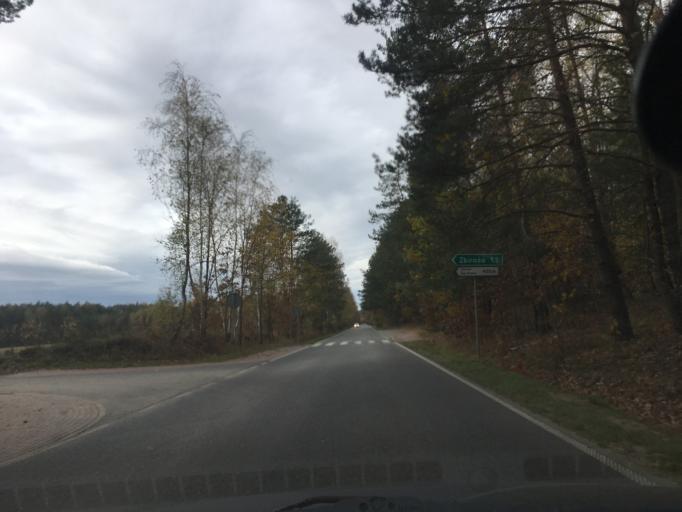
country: PL
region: Masovian Voivodeship
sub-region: Powiat zyrardowski
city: Radziejowice
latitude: 51.9670
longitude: 20.6011
